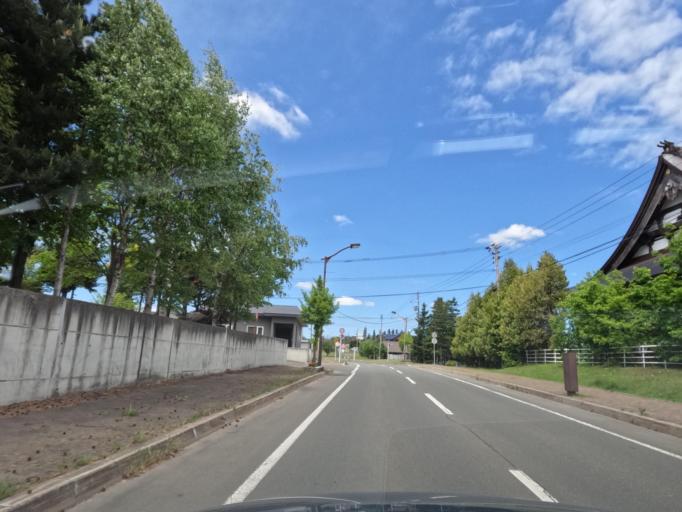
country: JP
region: Hokkaido
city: Shimo-furano
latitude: 43.4612
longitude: 142.4613
